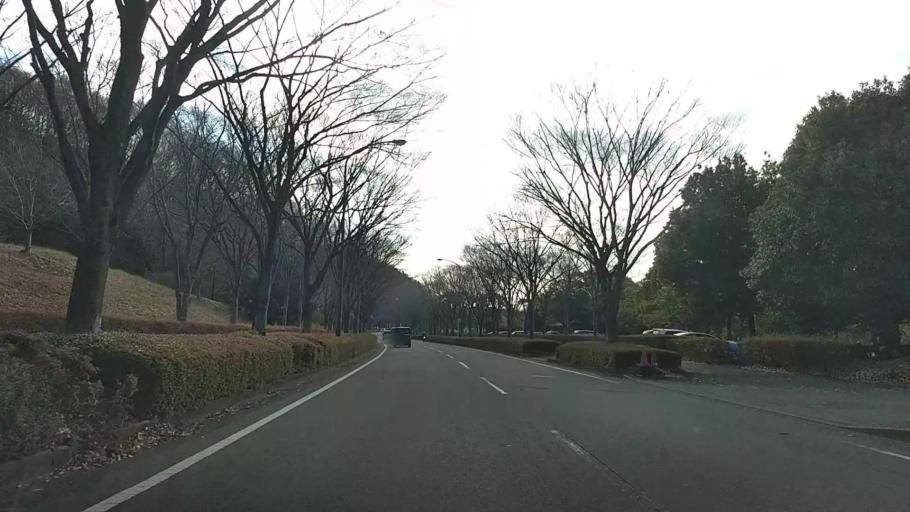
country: JP
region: Kanagawa
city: Atsugi
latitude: 35.4447
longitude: 139.3111
